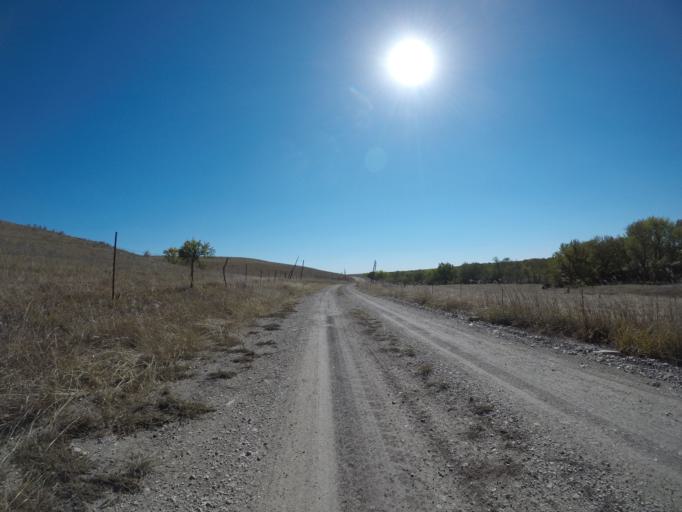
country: US
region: Kansas
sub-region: Wabaunsee County
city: Alma
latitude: 39.0192
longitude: -96.4104
